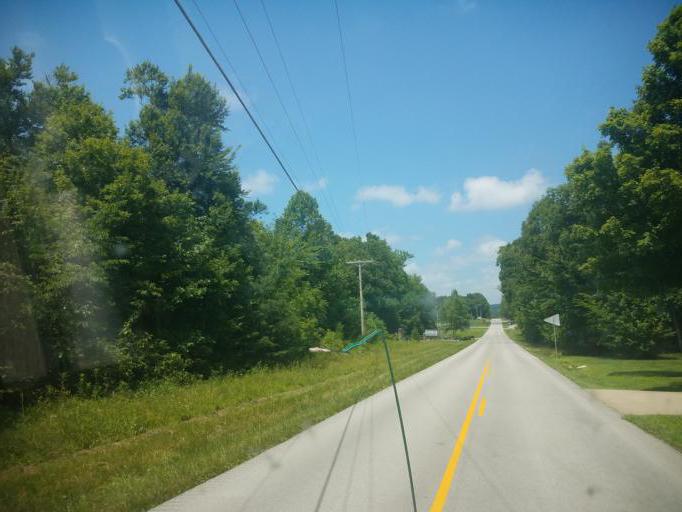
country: US
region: Kentucky
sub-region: Edmonson County
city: Brownsville
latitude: 37.3317
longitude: -86.1240
